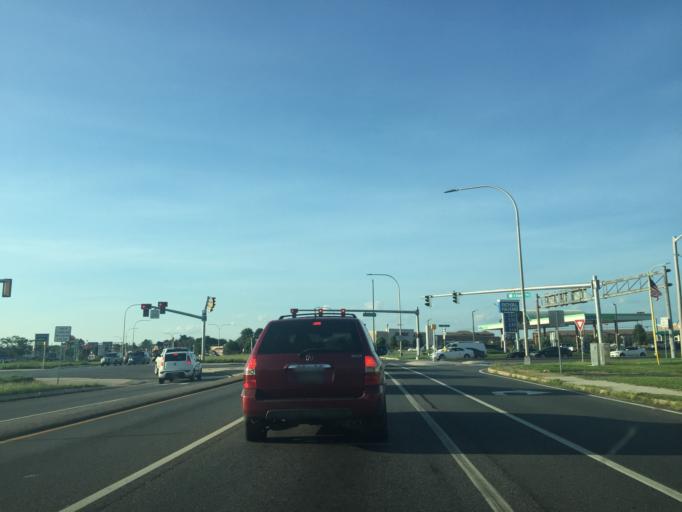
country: US
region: Delaware
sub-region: Kent County
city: Dover
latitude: 39.1570
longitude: -75.5121
